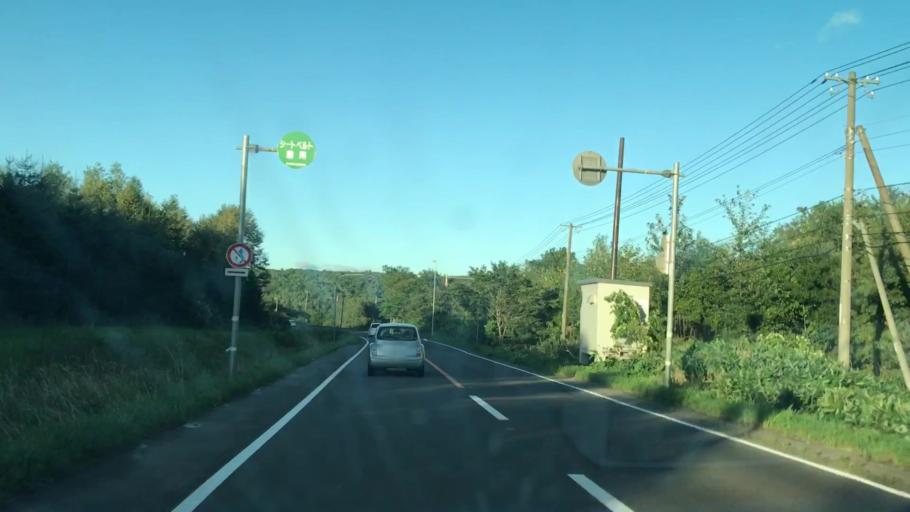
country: JP
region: Hokkaido
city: Niseko Town
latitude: 42.7558
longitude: 140.9234
